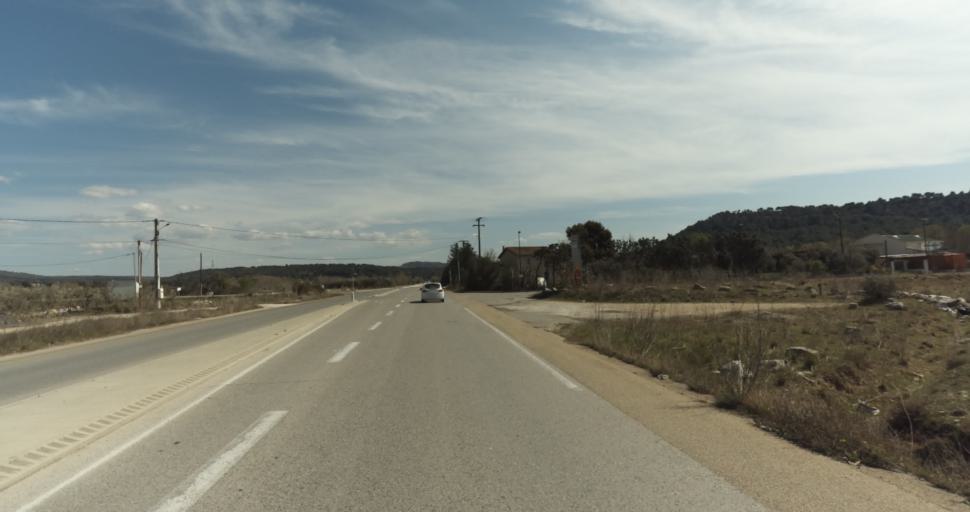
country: FR
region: Provence-Alpes-Cote d'Azur
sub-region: Departement des Bouches-du-Rhone
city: Coudoux
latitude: 43.5494
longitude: 5.2422
